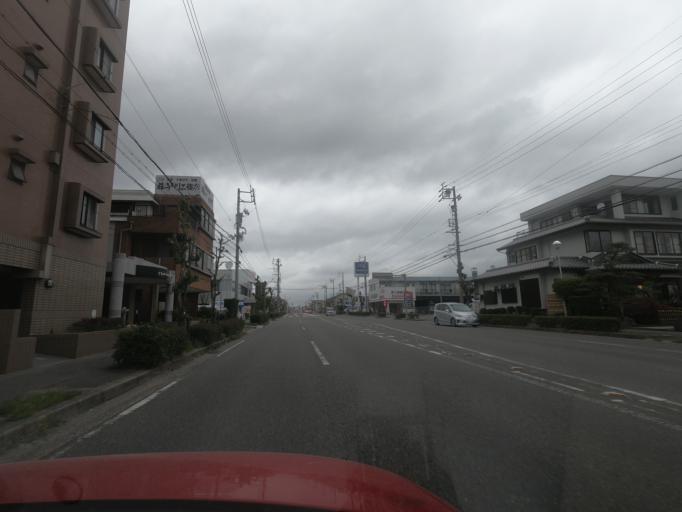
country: JP
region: Aichi
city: Kasugai
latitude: 35.2585
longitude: 136.9677
